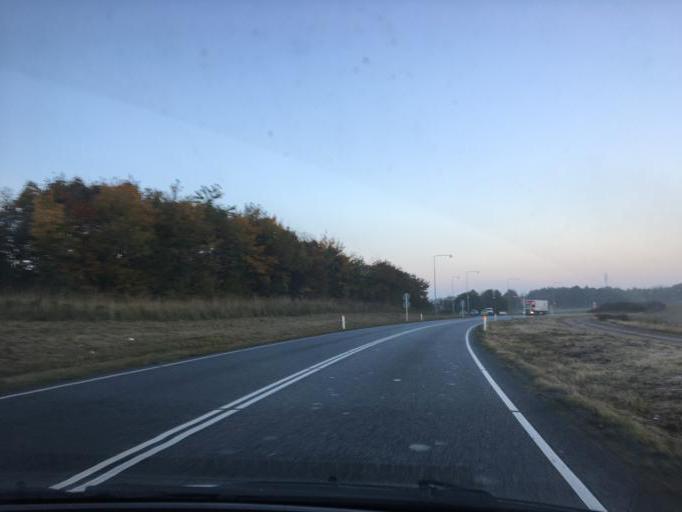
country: DK
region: South Denmark
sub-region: Vejle Kommune
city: Vejle
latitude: 55.6632
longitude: 9.5503
